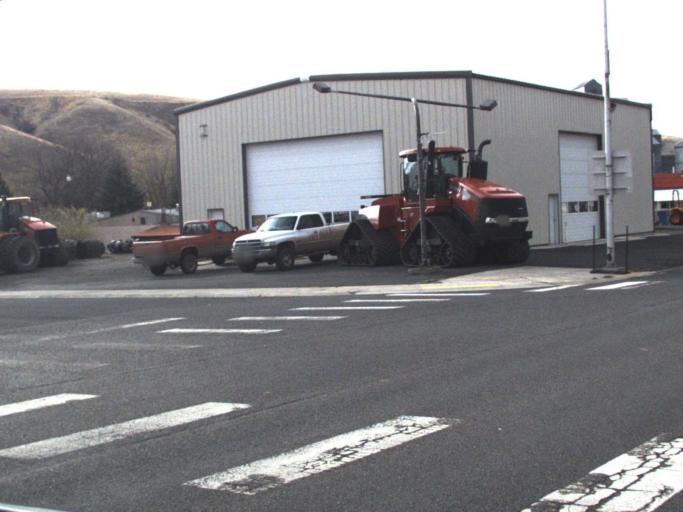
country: US
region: Washington
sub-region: Garfield County
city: Pomeroy
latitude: 46.4748
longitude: -117.6029
